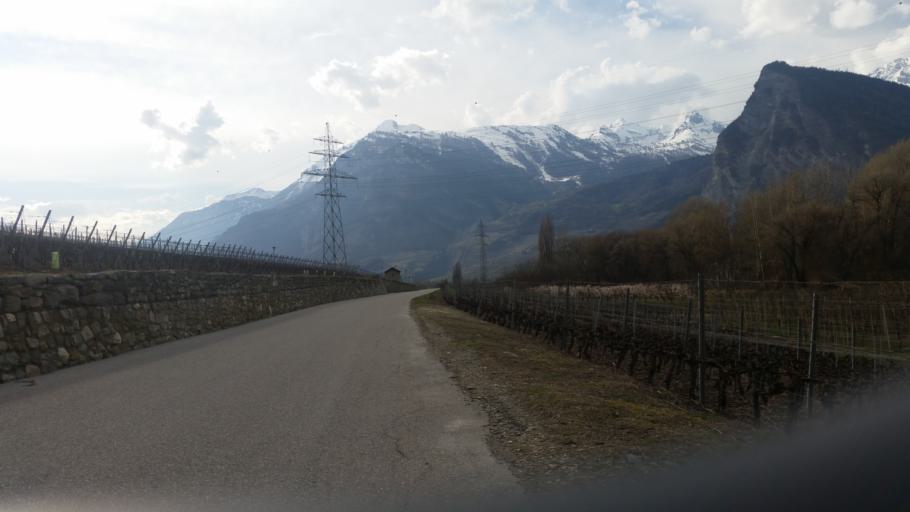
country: CH
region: Valais
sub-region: Martigny District
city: Riddes
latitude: 46.1802
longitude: 7.2454
